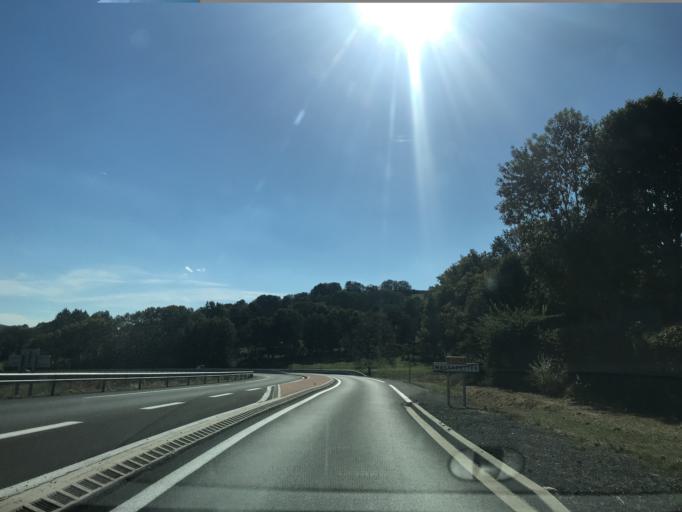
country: FR
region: Auvergne
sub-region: Departement du Puy-de-Dome
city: Gelles
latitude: 45.7350
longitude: 2.8145
